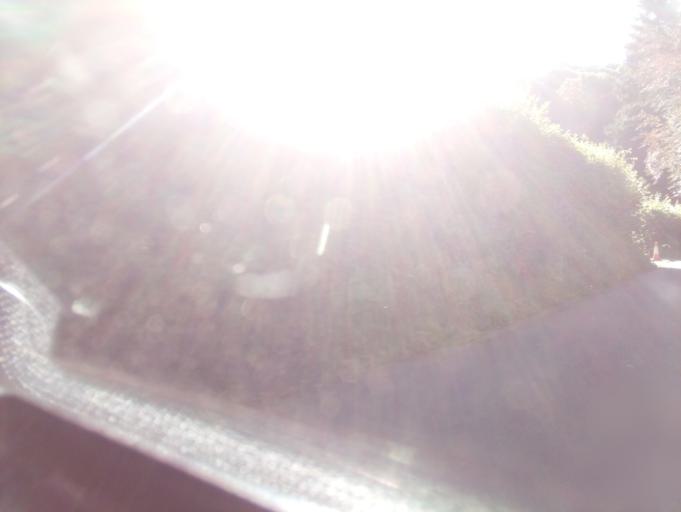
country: GB
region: Wales
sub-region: Monmouthshire
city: Tintern
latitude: 51.7119
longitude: -2.6866
